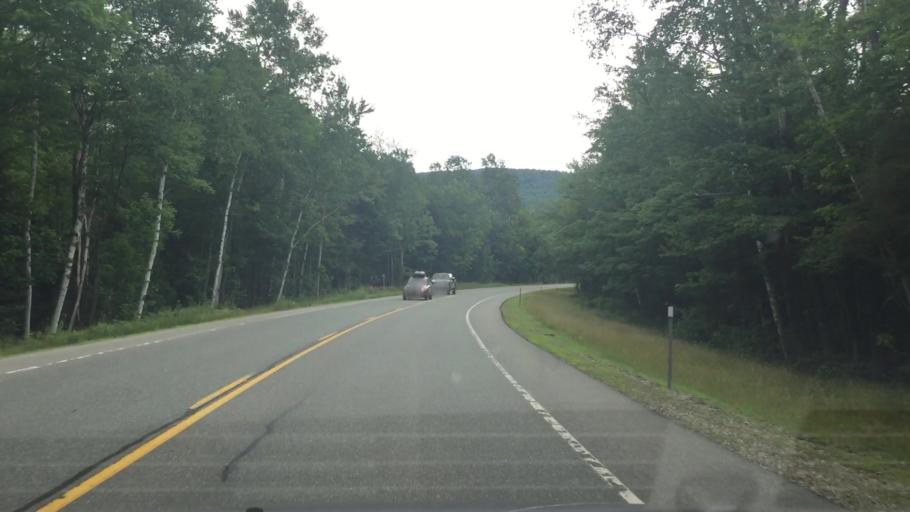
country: US
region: New Hampshire
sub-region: Grafton County
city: Deerfield
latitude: 44.2215
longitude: -71.6735
